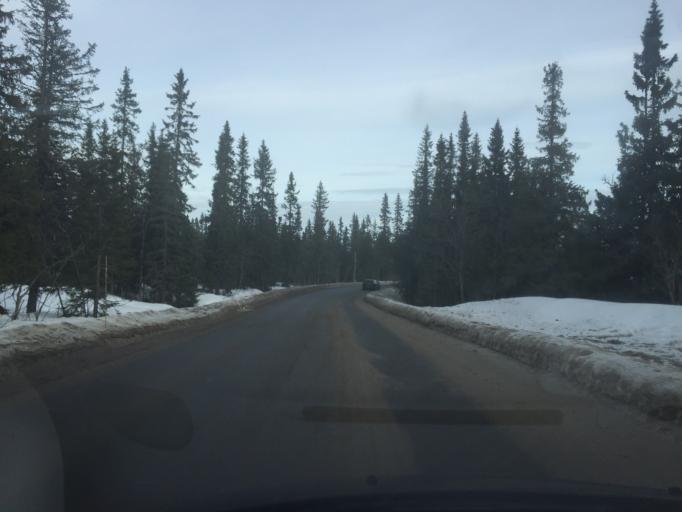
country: NO
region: Hedmark
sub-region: Trysil
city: Innbygda
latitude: 61.3347
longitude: 12.1729
